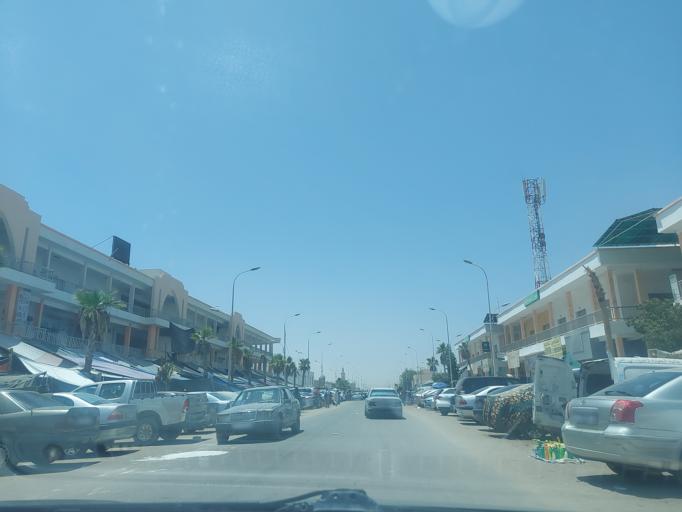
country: MR
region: Nouakchott
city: Nouakchott
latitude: 18.0852
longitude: -15.9808
